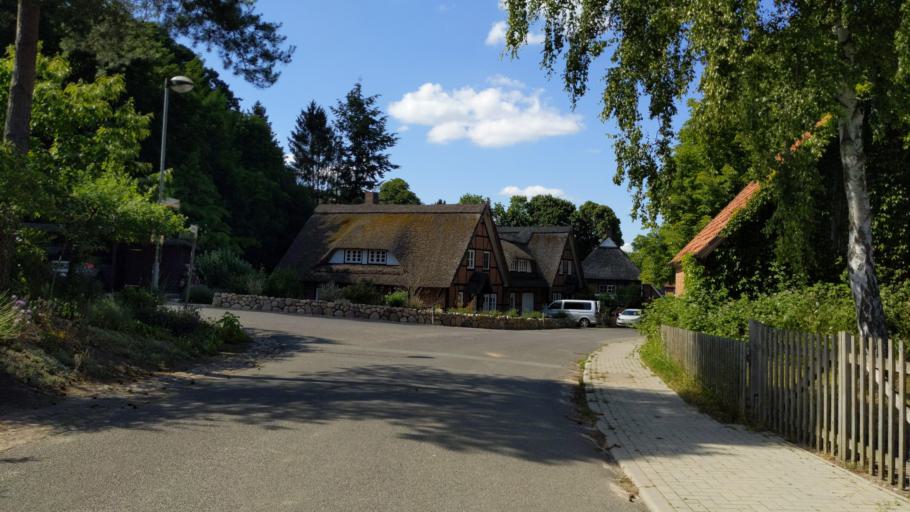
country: DE
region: Schleswig-Holstein
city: Kulpin
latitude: 53.7085
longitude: 10.6966
